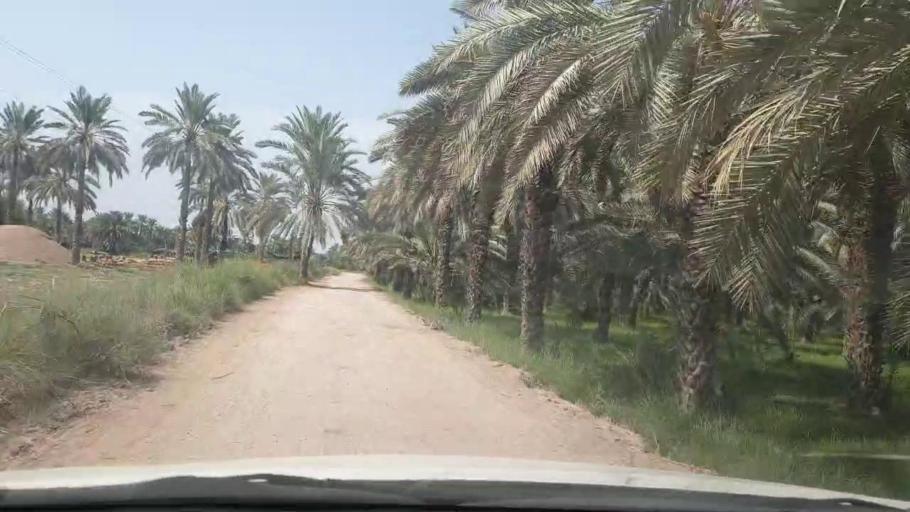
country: PK
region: Sindh
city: Khairpur
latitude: 27.5877
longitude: 68.8553
